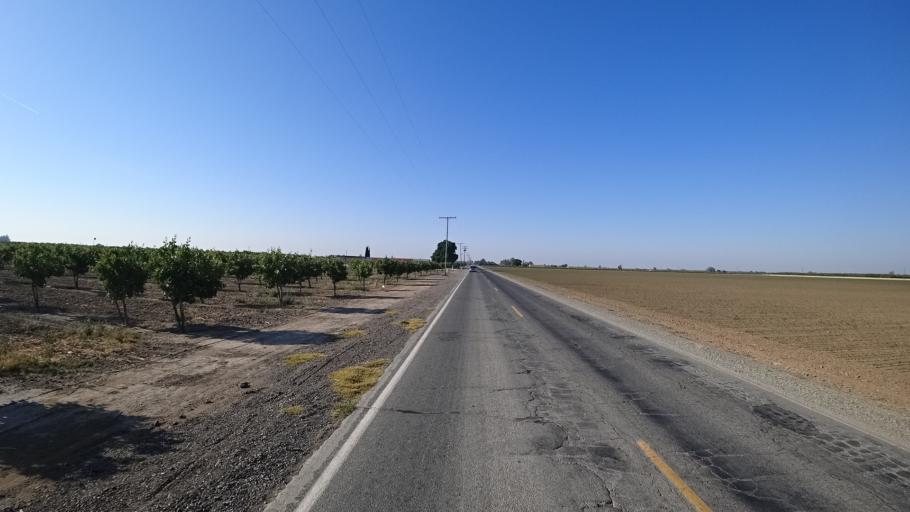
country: US
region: California
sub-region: Kings County
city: Armona
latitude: 36.2960
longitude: -119.7092
